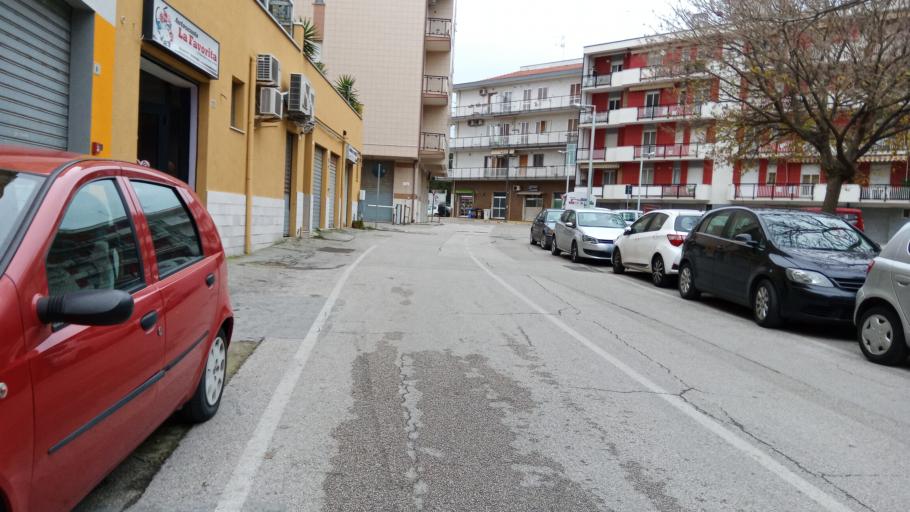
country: IT
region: Molise
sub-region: Provincia di Campobasso
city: Termoli
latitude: 41.9994
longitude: 14.9892
